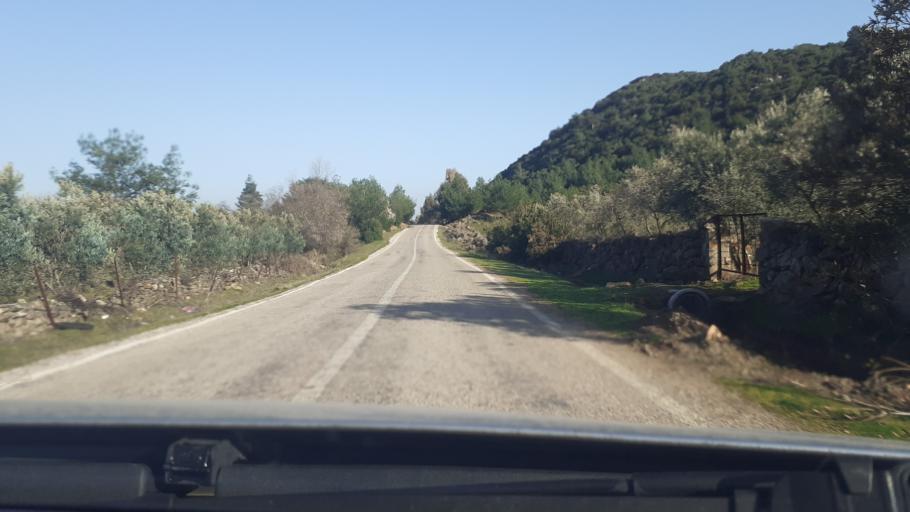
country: TR
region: Hatay
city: Aktepe
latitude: 36.7334
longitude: 36.4710
